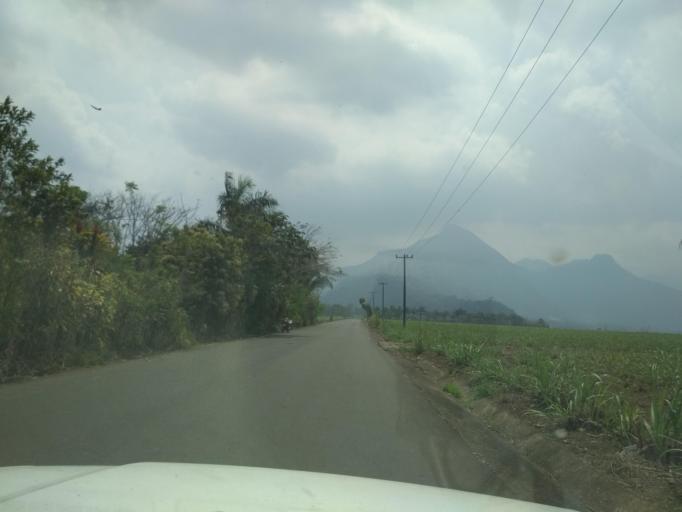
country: MX
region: Veracruz
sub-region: Cordoba
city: San Jose de Tapia
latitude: 18.8466
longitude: -96.9802
